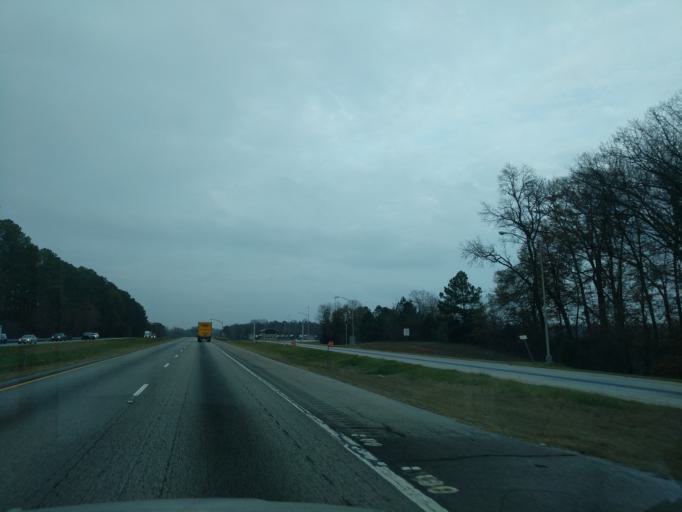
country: US
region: Georgia
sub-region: Franklin County
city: Lavonia
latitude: 34.4196
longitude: -83.1670
